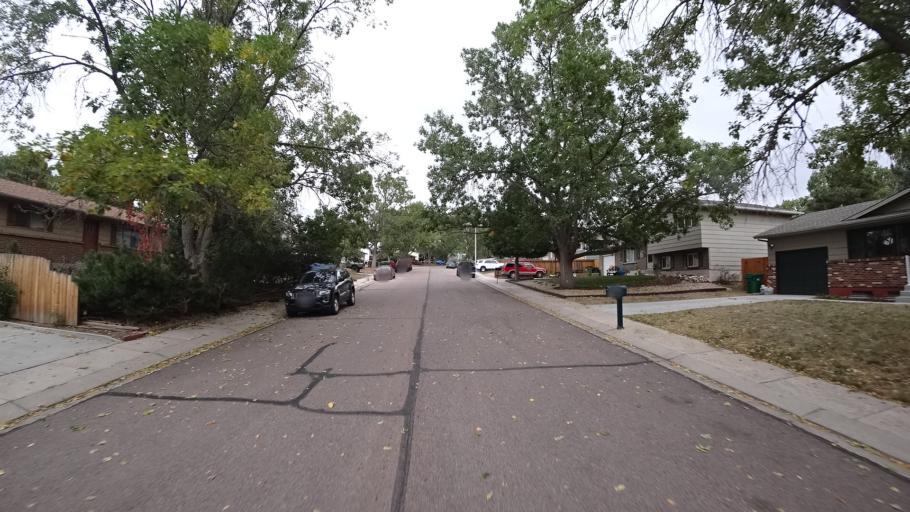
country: US
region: Colorado
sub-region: El Paso County
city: Cimarron Hills
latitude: 38.8953
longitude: -104.7404
